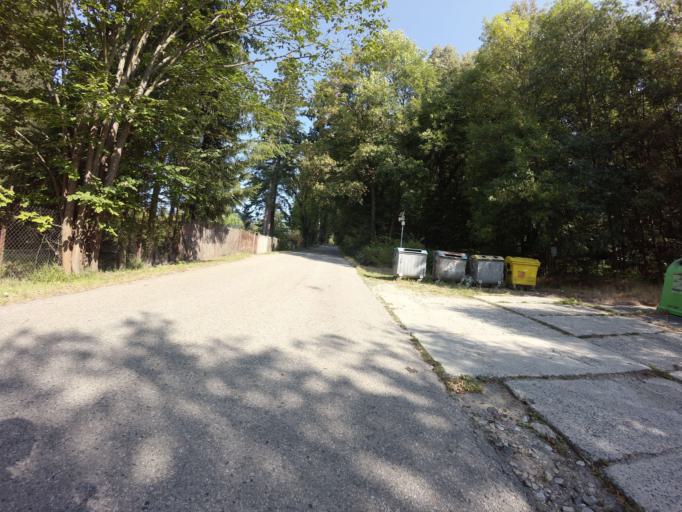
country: CZ
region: Jihocesky
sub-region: Okres Cesky Krumlov
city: Cesky Krumlov
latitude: 48.8318
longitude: 14.3115
